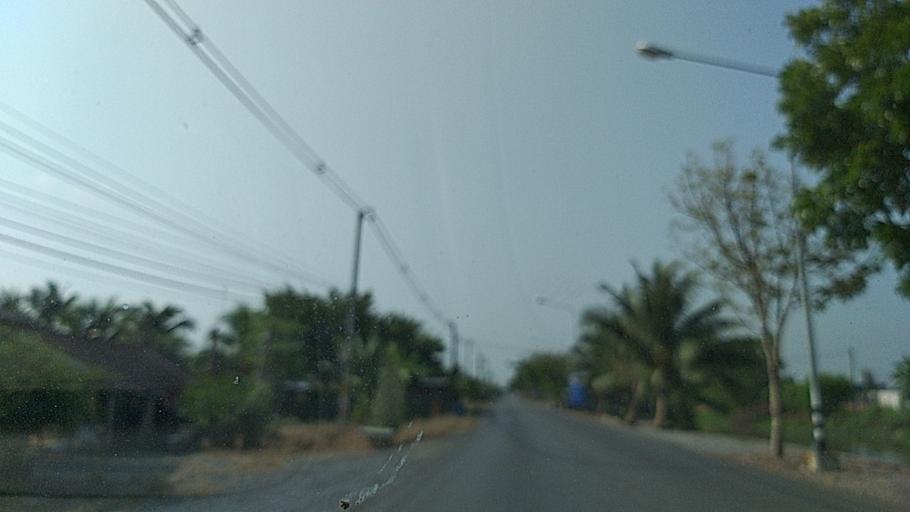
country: TH
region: Pathum Thani
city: Lam Luk Ka
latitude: 13.9642
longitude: 100.7060
